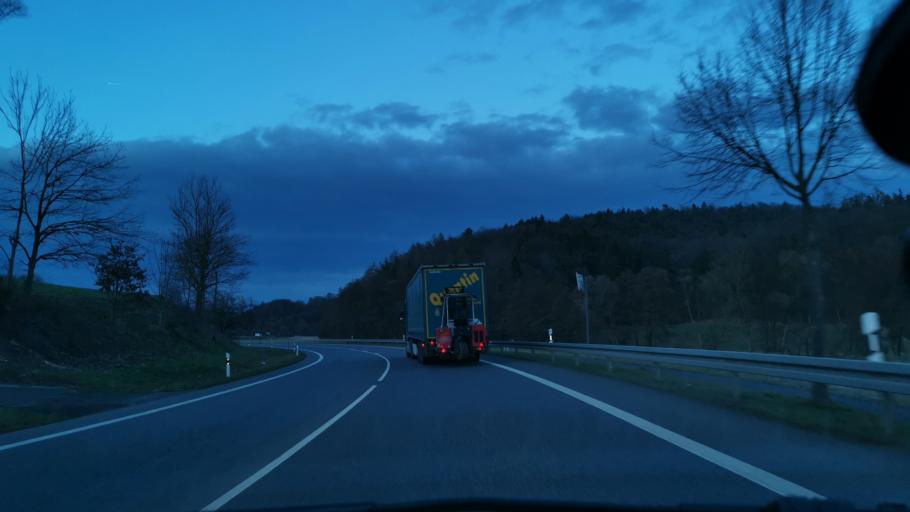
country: DE
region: Hesse
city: Bebra
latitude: 50.9950
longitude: 9.8108
